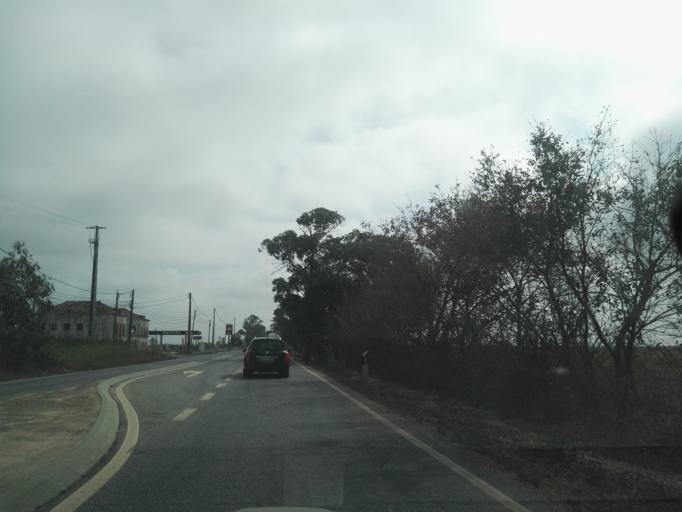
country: PT
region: Lisbon
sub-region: Vila Franca de Xira
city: Vila Franca de Xira
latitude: 38.9430
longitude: -8.9478
